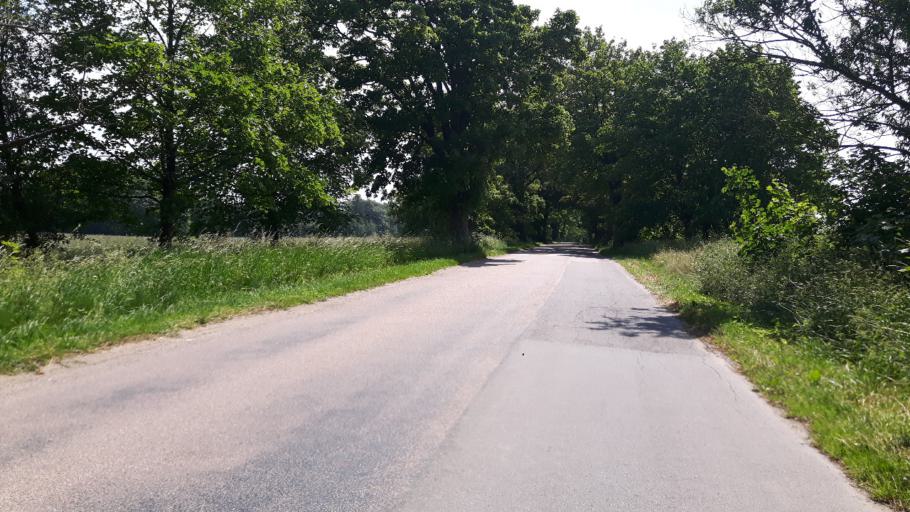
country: PL
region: Pomeranian Voivodeship
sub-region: Powiat wejherowski
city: Choczewo
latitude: 54.7435
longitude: 17.8109
